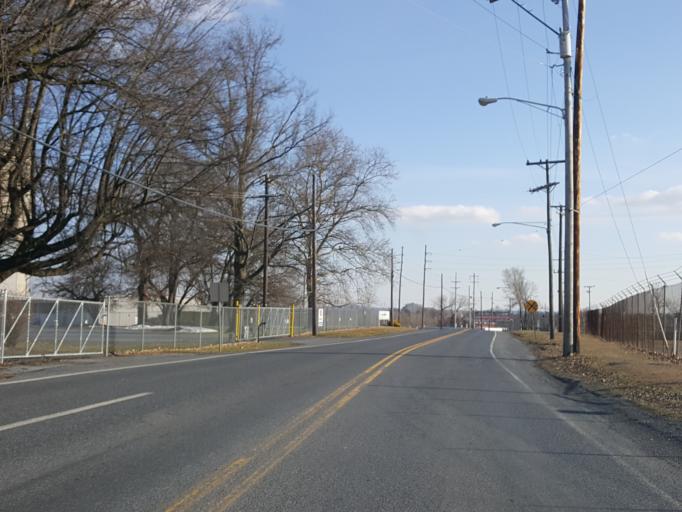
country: US
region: Pennsylvania
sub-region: Lebanon County
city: Pleasant Hill
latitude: 40.3443
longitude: -76.4414
